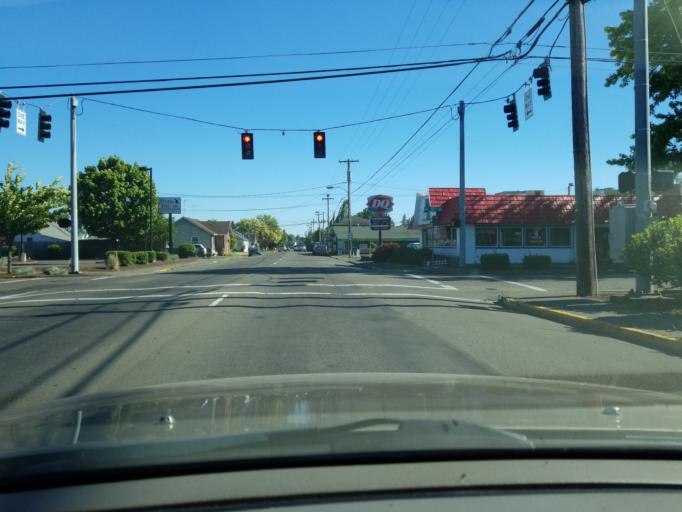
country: US
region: Oregon
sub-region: Yamhill County
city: McMinnville
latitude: 45.2167
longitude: -123.1990
